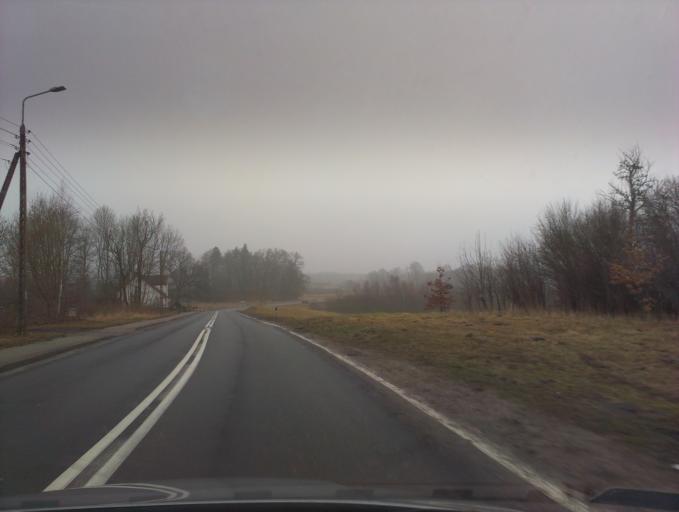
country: PL
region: West Pomeranian Voivodeship
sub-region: Powiat koszalinski
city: Bobolice
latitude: 53.8649
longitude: 16.6115
